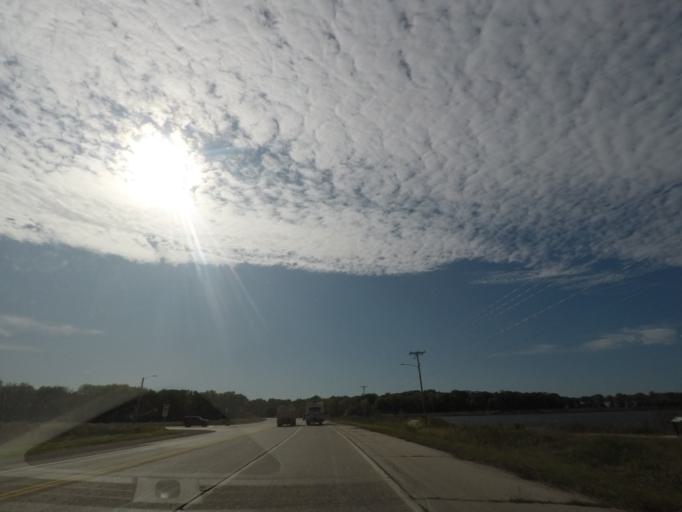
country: US
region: Iowa
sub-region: Story County
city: Ames
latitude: 42.0669
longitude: -93.6232
